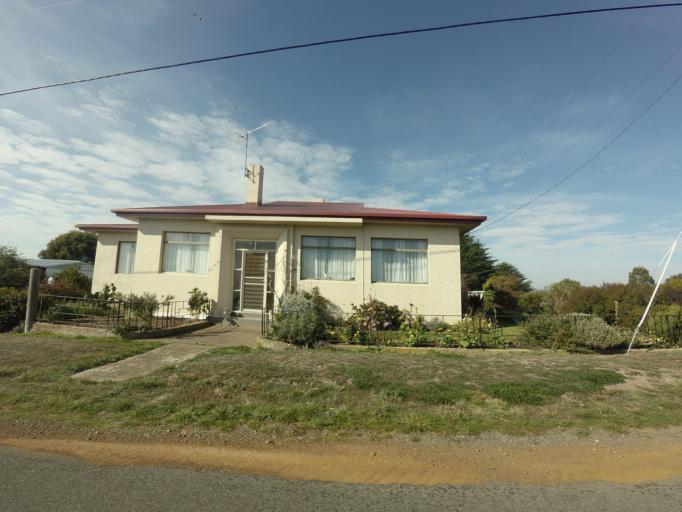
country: AU
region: Tasmania
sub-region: Sorell
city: Sorell
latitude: -42.4531
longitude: 147.4616
